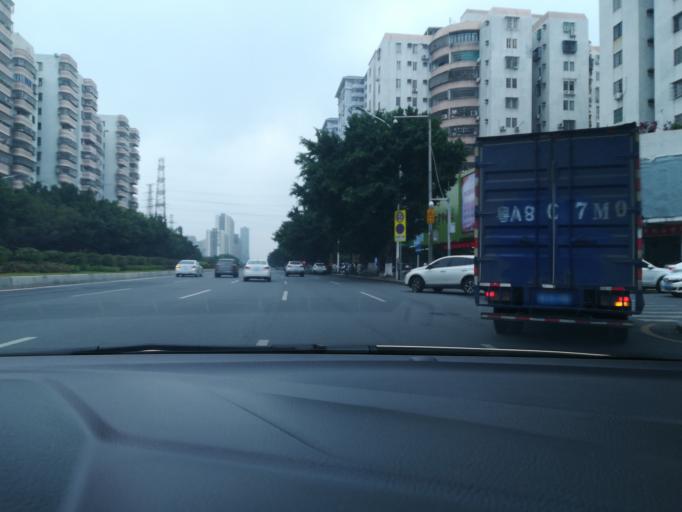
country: CN
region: Guangdong
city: Nansha
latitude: 22.8006
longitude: 113.5555
